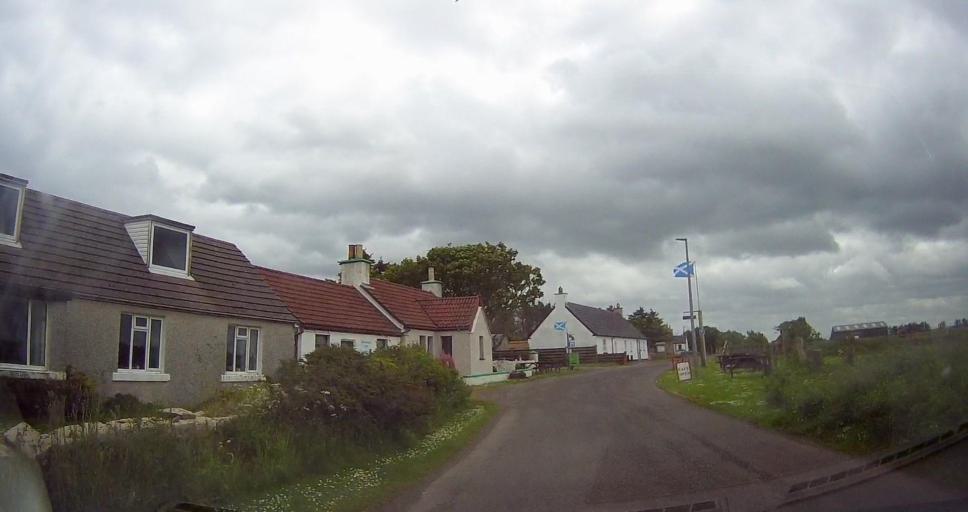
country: GB
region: Scotland
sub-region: Highland
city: Thurso
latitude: 58.6459
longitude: -3.3453
